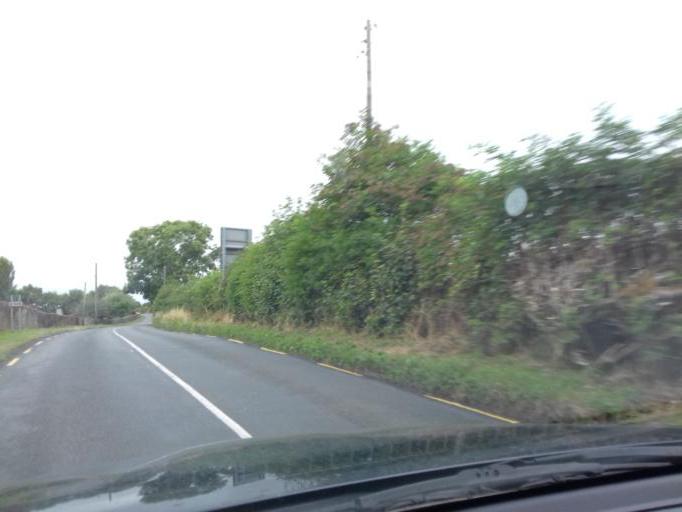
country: IE
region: Leinster
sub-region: County Carlow
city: Bagenalstown
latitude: 52.7150
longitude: -6.9598
